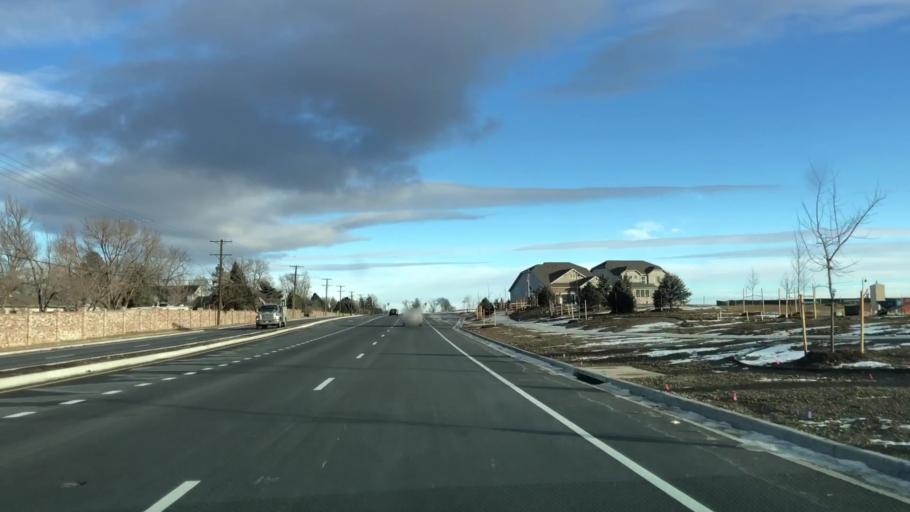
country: US
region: Colorado
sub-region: Larimer County
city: Loveland
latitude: 40.4228
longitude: -105.0207
